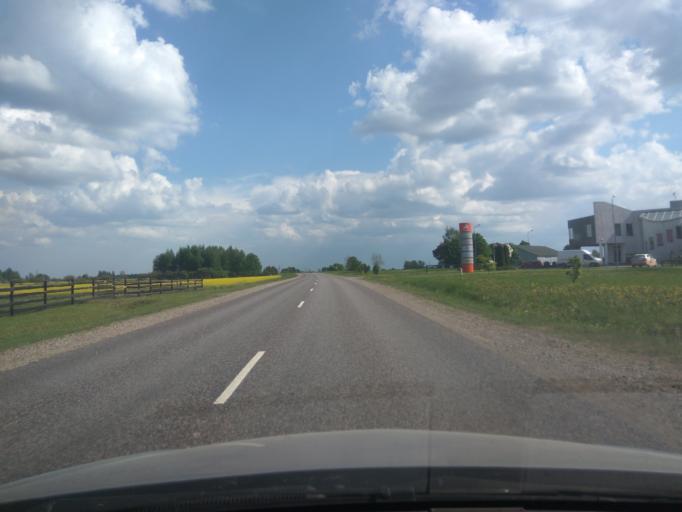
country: LV
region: Kuldigas Rajons
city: Kuldiga
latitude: 56.9988
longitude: 21.8995
